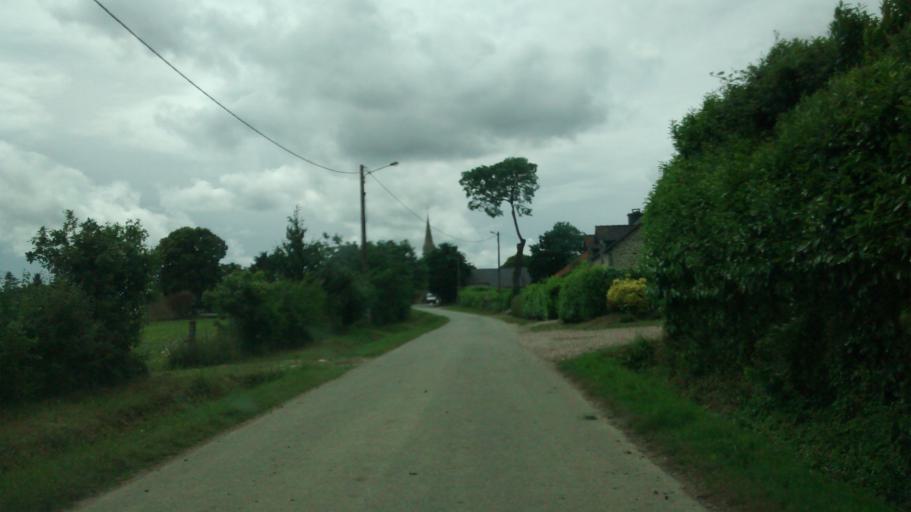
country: FR
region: Brittany
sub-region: Departement du Morbihan
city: Ruffiac
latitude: 47.8394
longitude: -2.2197
